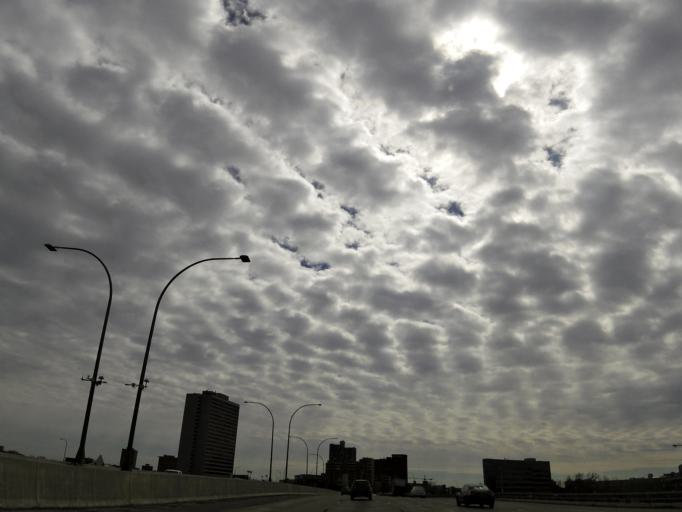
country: US
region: Minnesota
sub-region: Hennepin County
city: Minneapolis
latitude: 44.9795
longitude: -93.2449
